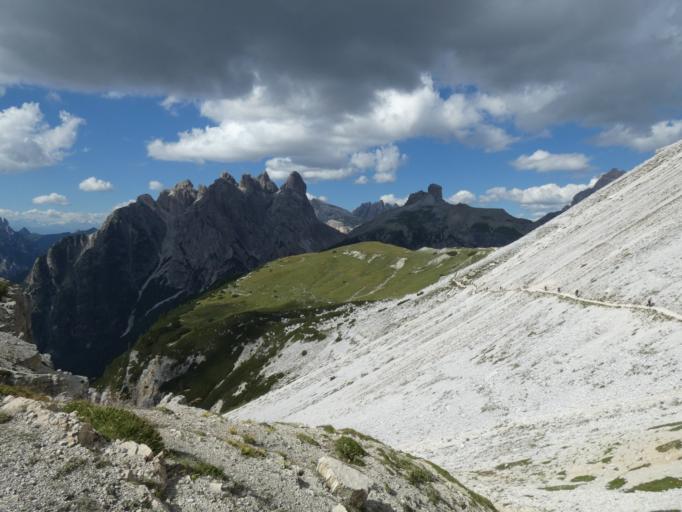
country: IT
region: Trentino-Alto Adige
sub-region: Bolzano
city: Sesto
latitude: 46.6175
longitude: 12.2845
